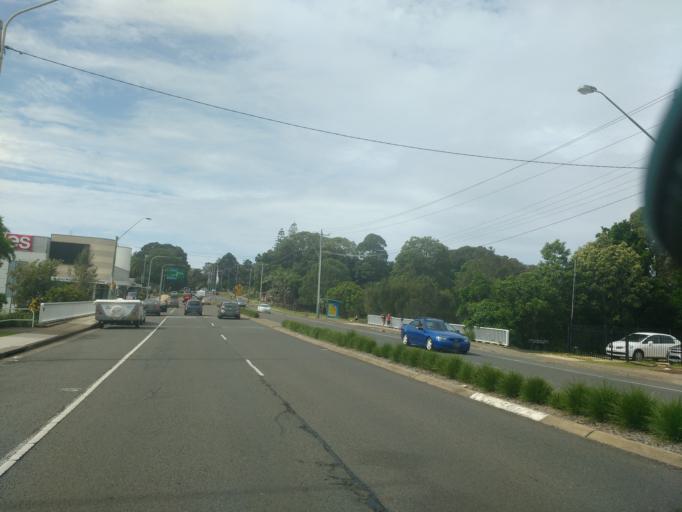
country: AU
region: New South Wales
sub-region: Port Macquarie-Hastings
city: Port Macquarie
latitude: -31.4345
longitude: 152.9060
